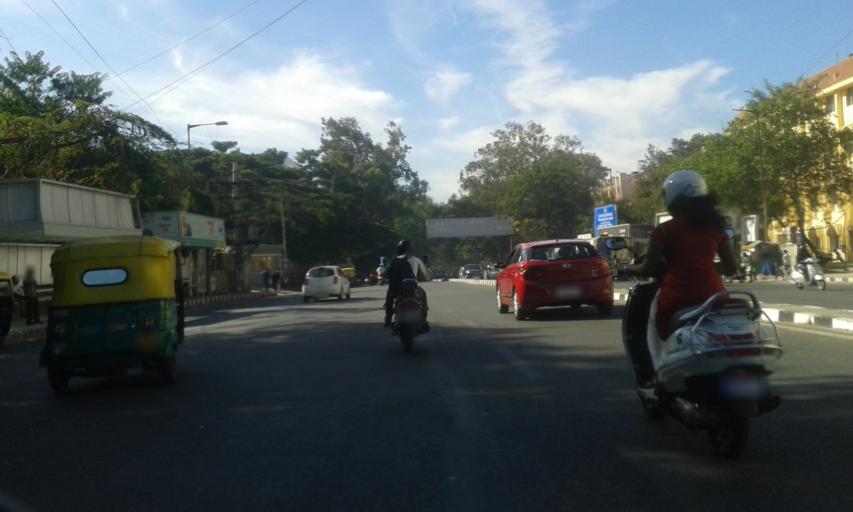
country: IN
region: Karnataka
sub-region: Bangalore Urban
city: Bangalore
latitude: 12.9359
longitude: 77.6014
